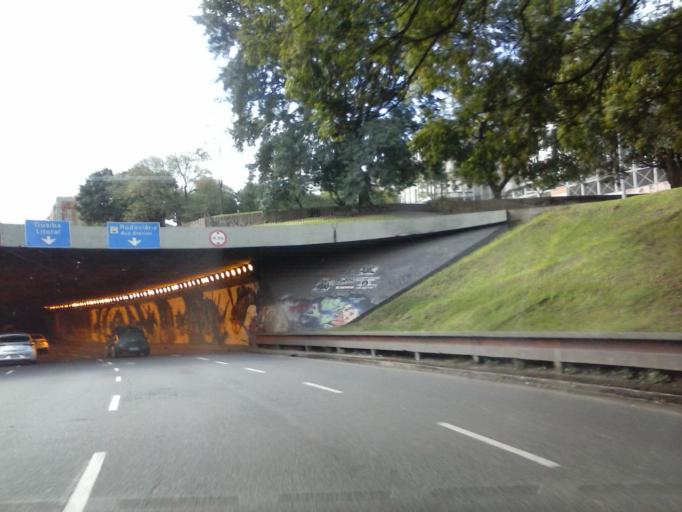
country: BR
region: Rio Grande do Sul
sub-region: Porto Alegre
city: Porto Alegre
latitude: -30.0315
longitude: -51.2190
